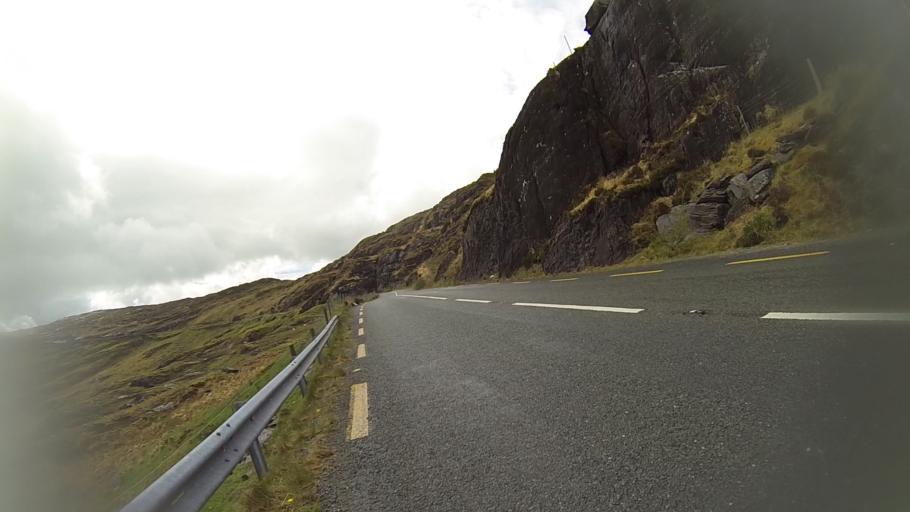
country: IE
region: Munster
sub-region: Ciarrai
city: Kenmare
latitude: 51.7917
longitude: -9.5923
